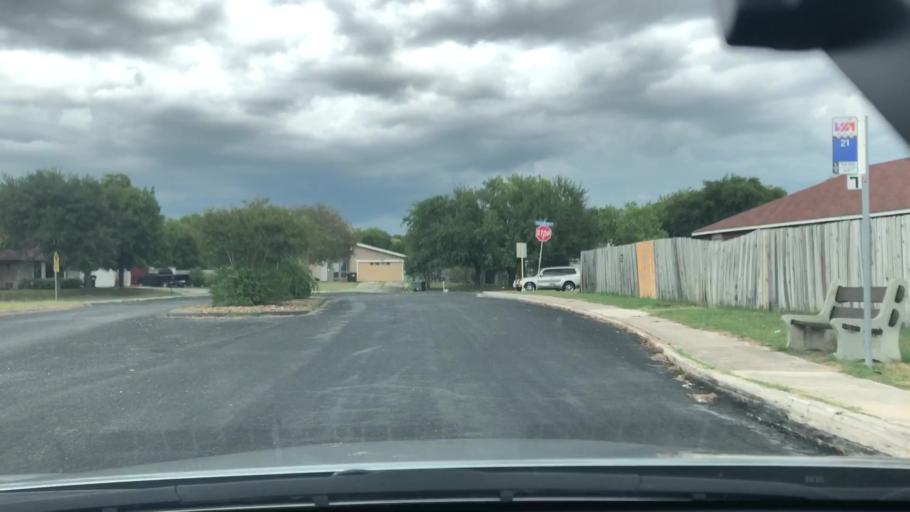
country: US
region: Texas
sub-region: Bexar County
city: Kirby
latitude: 29.4795
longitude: -98.3571
